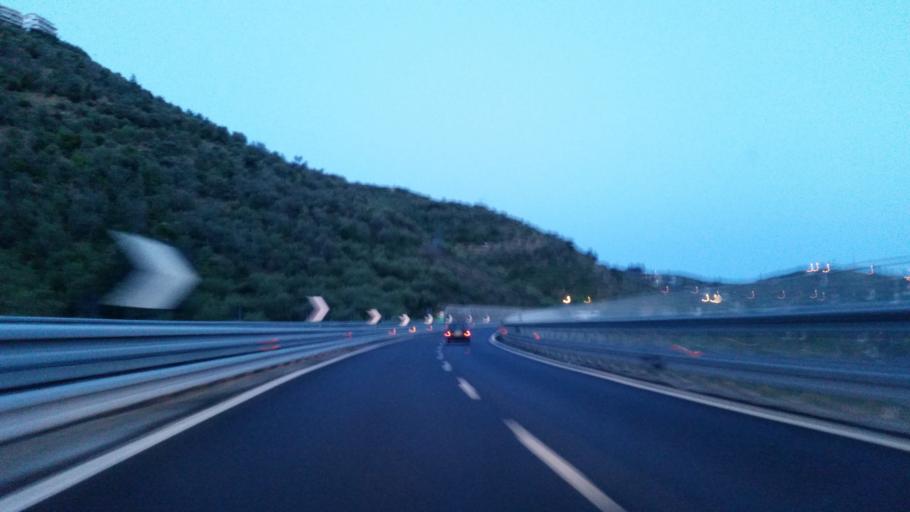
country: IT
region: Liguria
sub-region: Provincia di Imperia
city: Castellaro
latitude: 43.8699
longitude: 7.8591
